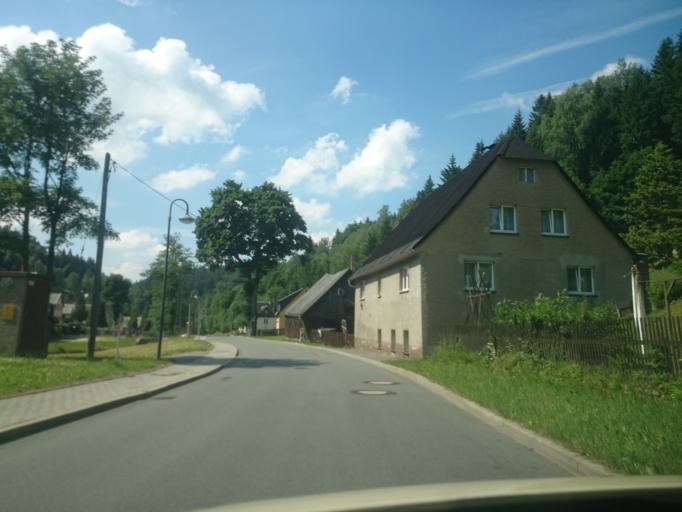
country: DE
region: Saxony
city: Pobershau
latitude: 50.6490
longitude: 13.2072
